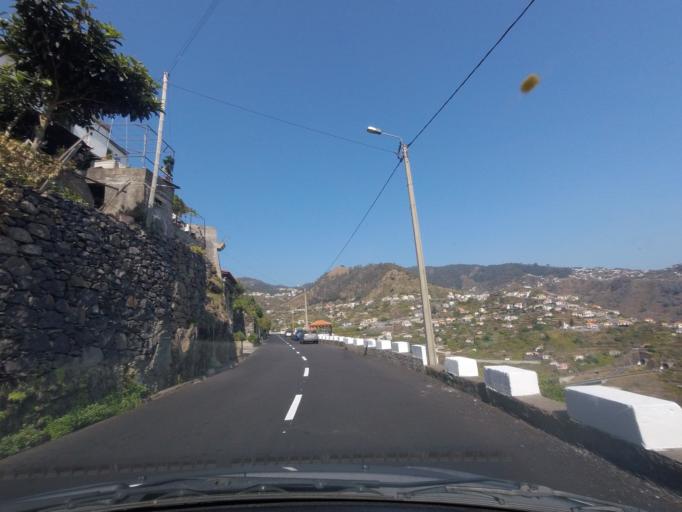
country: PT
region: Madeira
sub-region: Ribeira Brava
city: Campanario
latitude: 32.6682
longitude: -17.0466
